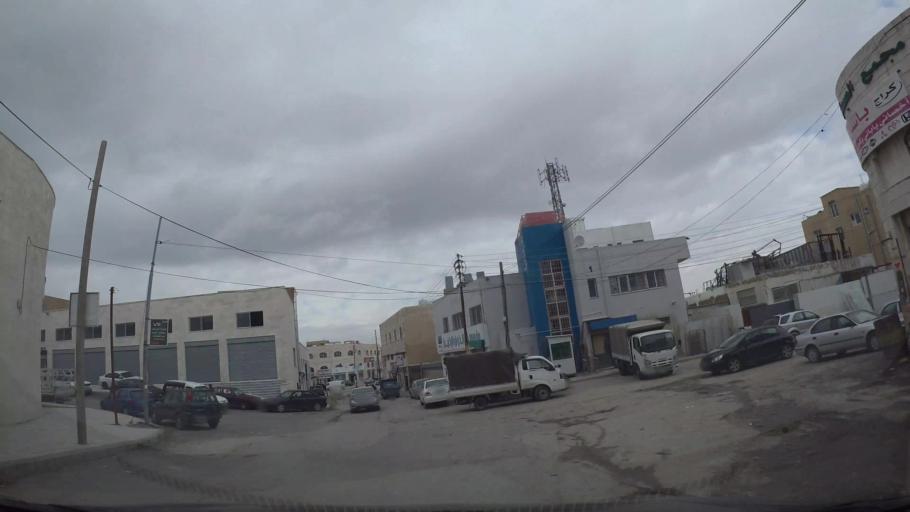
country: JO
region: Amman
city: Wadi as Sir
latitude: 31.9424
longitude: 35.8387
